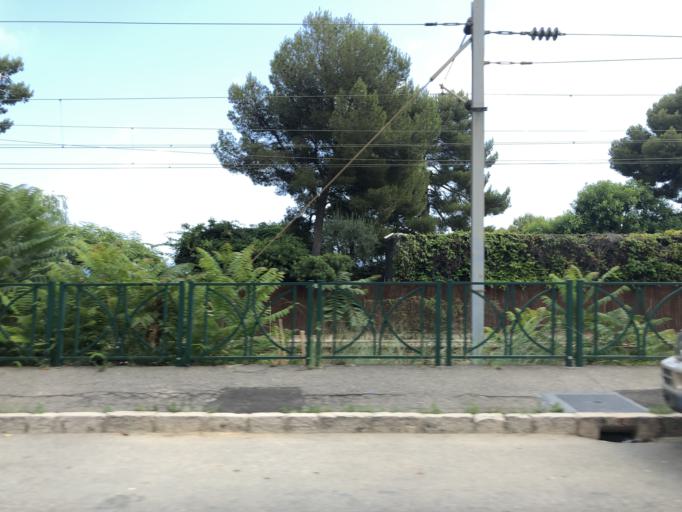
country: FR
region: Provence-Alpes-Cote d'Azur
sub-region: Departement des Alpes-Maritimes
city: Eze
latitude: 43.7214
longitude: 7.3550
